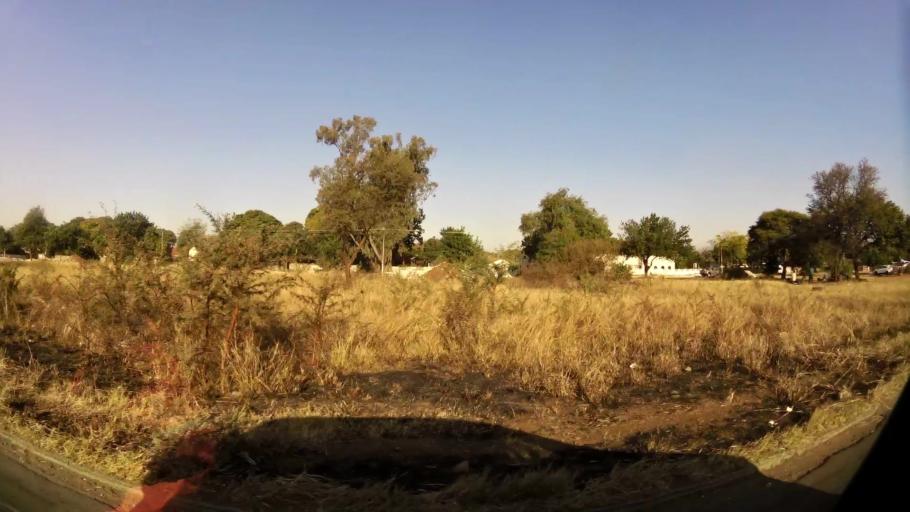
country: ZA
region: North-West
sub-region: Bojanala Platinum District Municipality
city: Rustenburg
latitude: -25.6479
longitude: 27.2260
